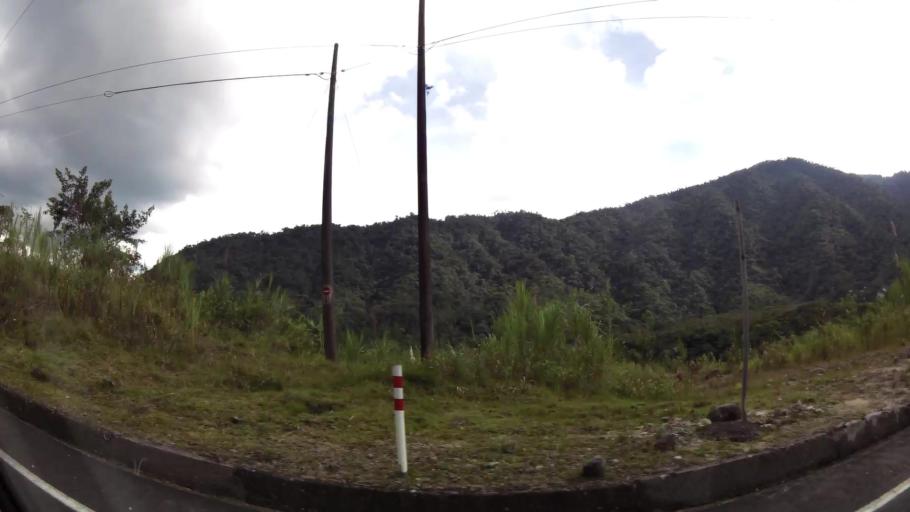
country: EC
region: Pastaza
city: Puyo
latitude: -1.4510
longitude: -78.1537
